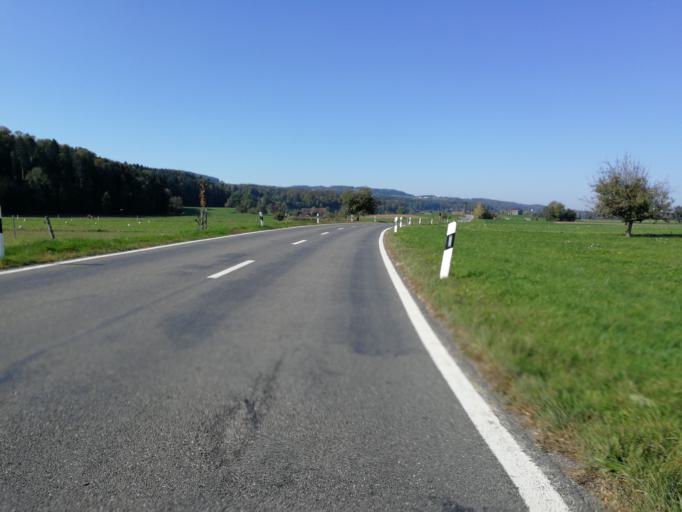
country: CH
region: Zurich
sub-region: Bezirk Uster
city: Monchaltorf
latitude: 47.3104
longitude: 8.7109
